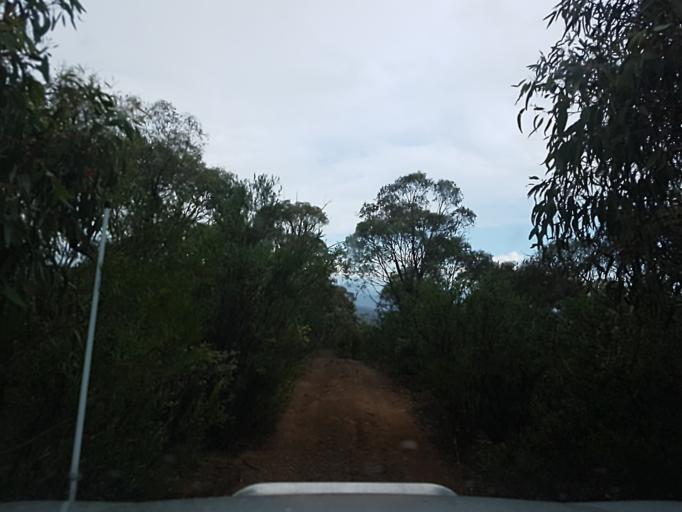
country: AU
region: New South Wales
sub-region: Snowy River
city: Jindabyne
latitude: -36.9217
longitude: 148.3418
